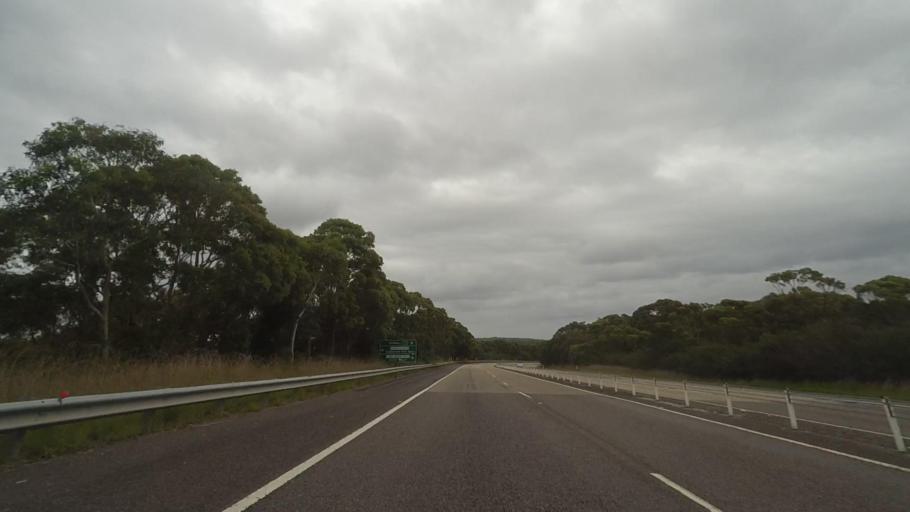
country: AU
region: New South Wales
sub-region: Lake Macquarie Shire
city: Arcadia vale
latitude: -33.1295
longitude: 151.6294
